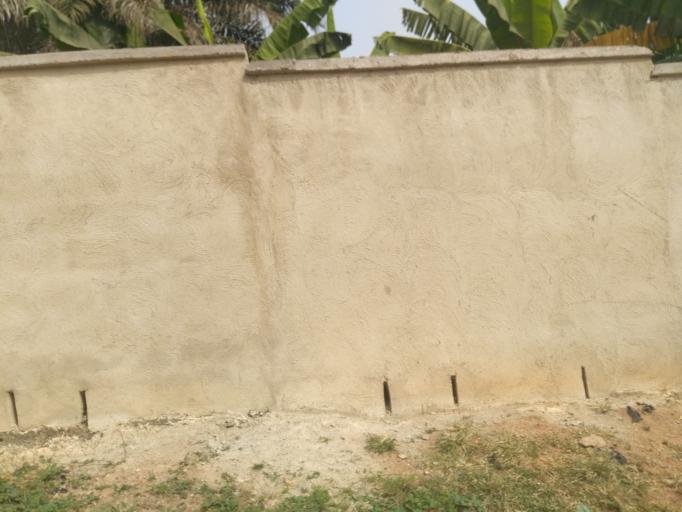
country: GH
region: Ashanti
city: Kumasi
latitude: 6.6916
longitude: -1.6031
